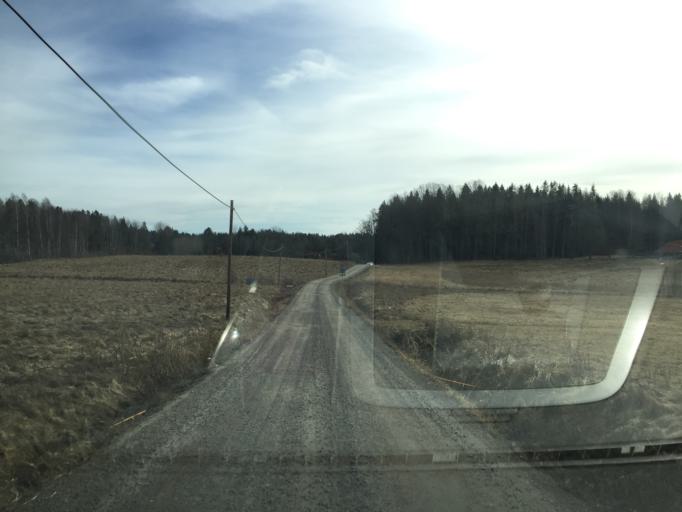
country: SE
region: Stockholm
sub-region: Botkyrka Kommun
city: Tullinge
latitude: 59.1013
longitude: 17.9663
